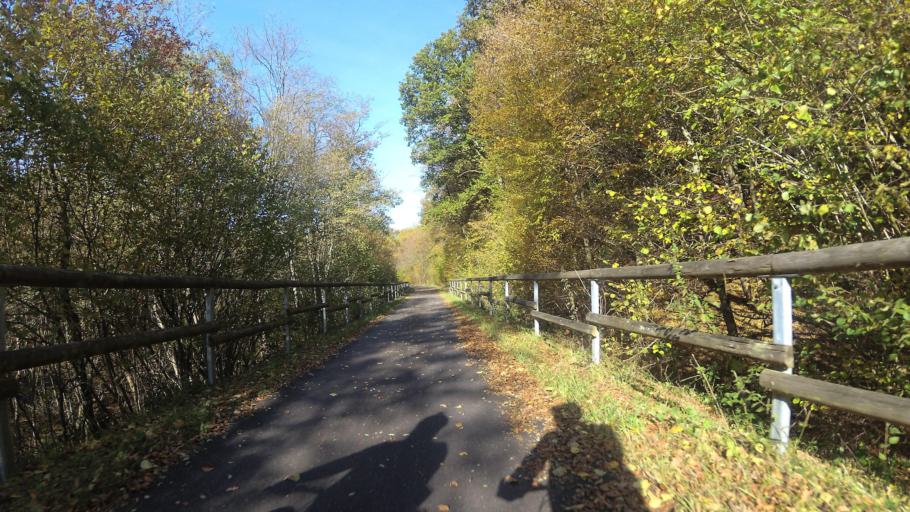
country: DE
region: Rheinland-Pfalz
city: Ollmuth
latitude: 49.6564
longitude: 6.7199
